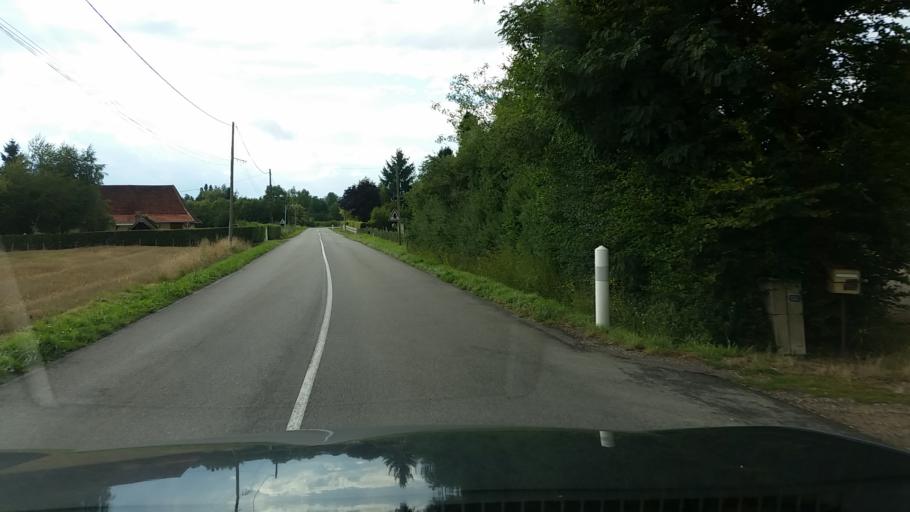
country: FR
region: Bourgogne
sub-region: Departement de Saone-et-Loire
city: Saint-Germain-du-Bois
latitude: 46.7406
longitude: 5.2512
